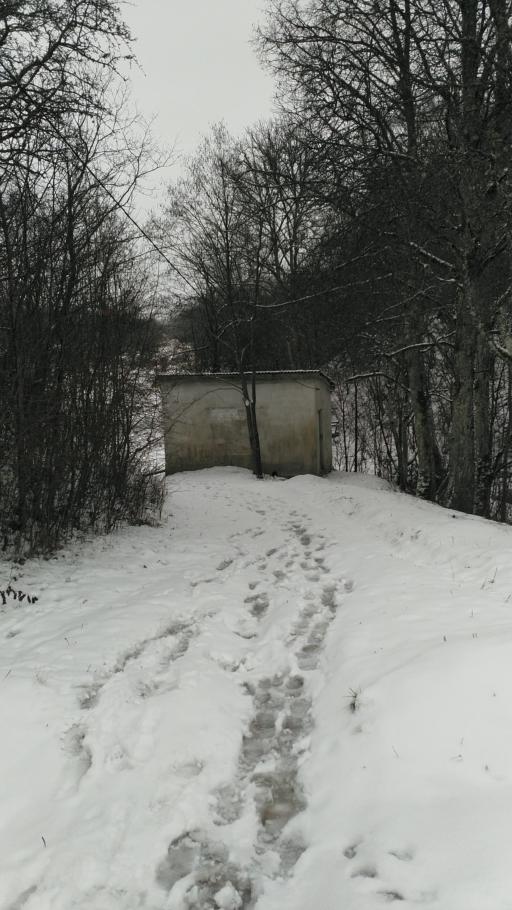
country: LV
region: Kuldigas Rajons
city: Kuldiga
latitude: 56.9514
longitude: 22.0035
